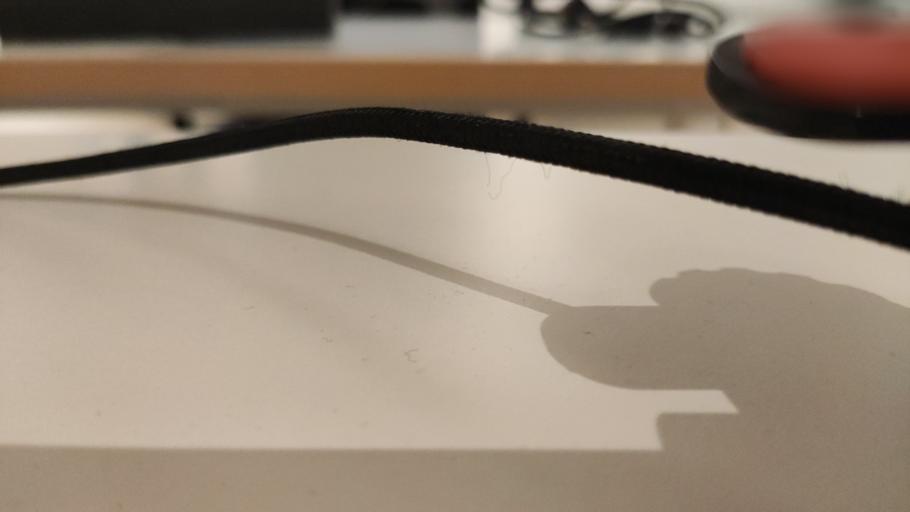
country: RU
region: Moskovskaya
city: Dorokhovo
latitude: 55.4064
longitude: 36.3760
